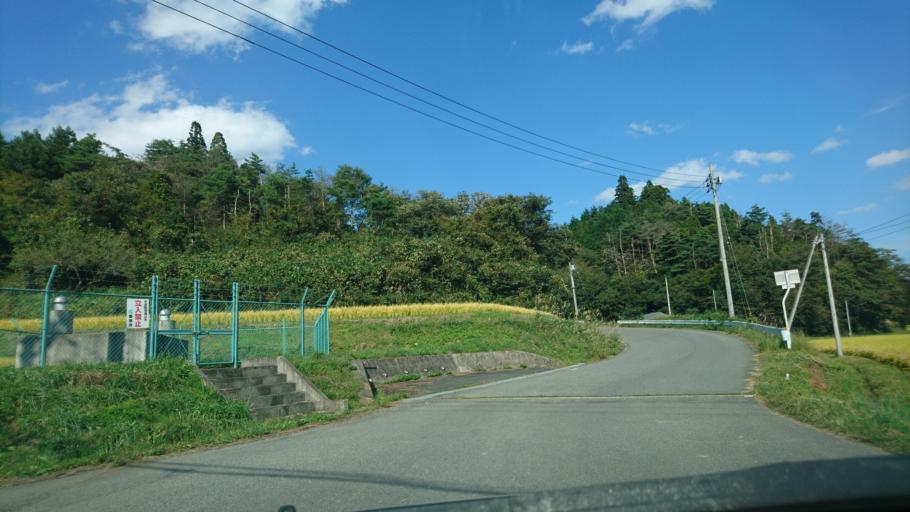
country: JP
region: Iwate
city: Ichinoseki
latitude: 38.8670
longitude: 141.0445
